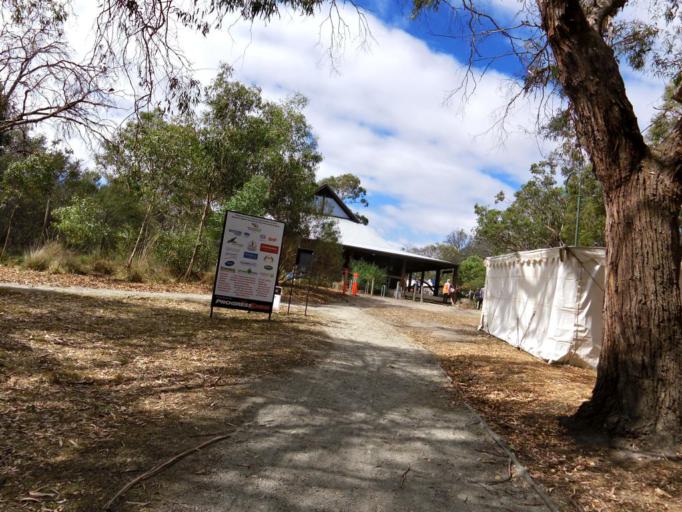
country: AU
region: Victoria
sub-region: Mornington Peninsula
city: Mount Martha
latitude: -38.2680
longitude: 145.0429
